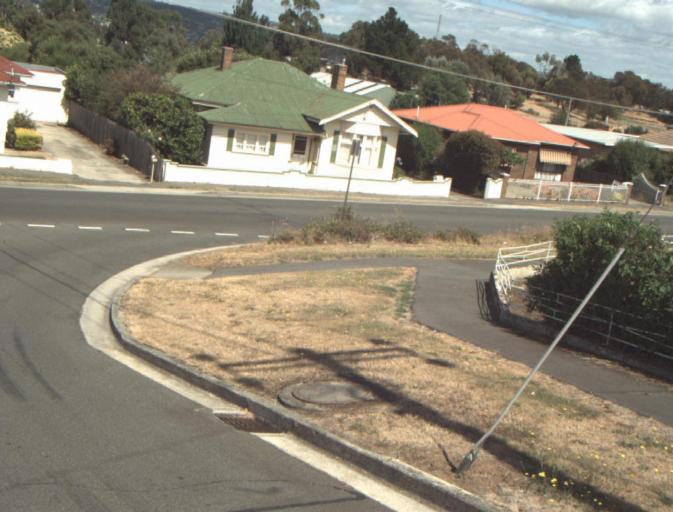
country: AU
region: Tasmania
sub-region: Launceston
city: Newstead
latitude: -41.4230
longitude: 147.1728
